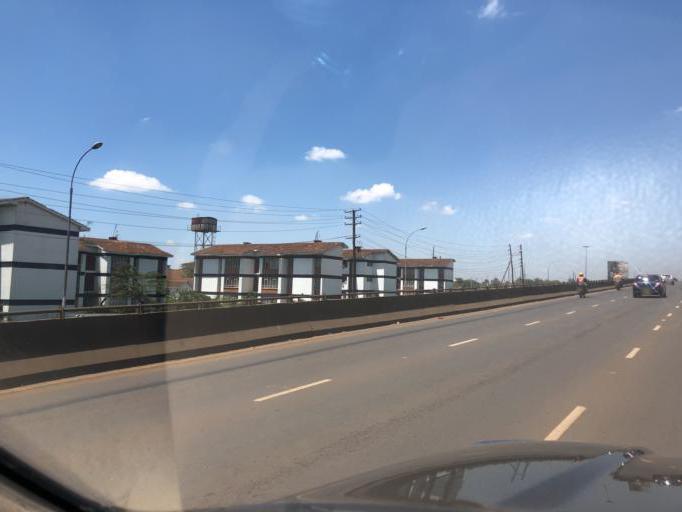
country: KE
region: Nairobi Area
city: Pumwani
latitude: -1.2180
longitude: 36.8933
